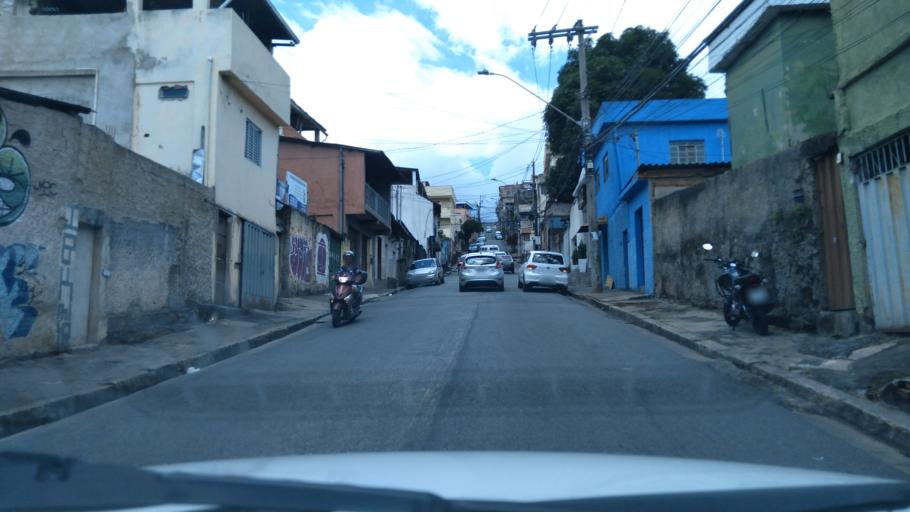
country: BR
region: Minas Gerais
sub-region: Belo Horizonte
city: Belo Horizonte
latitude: -19.9100
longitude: -43.8932
